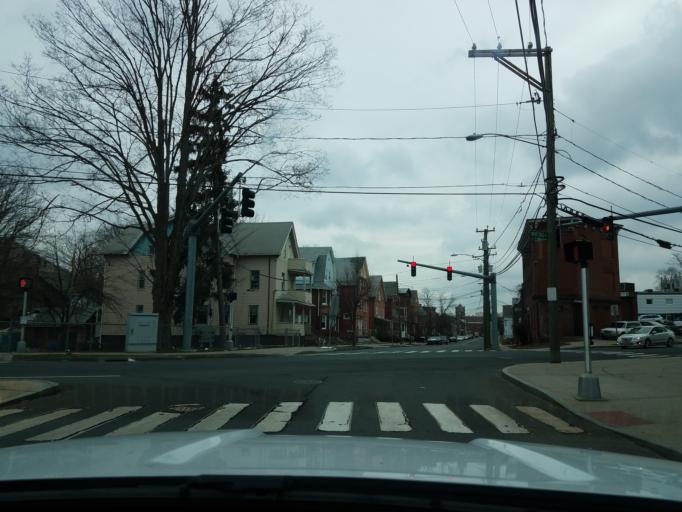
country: US
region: Connecticut
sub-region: Hartford County
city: New Britain
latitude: 41.6605
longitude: -72.7818
